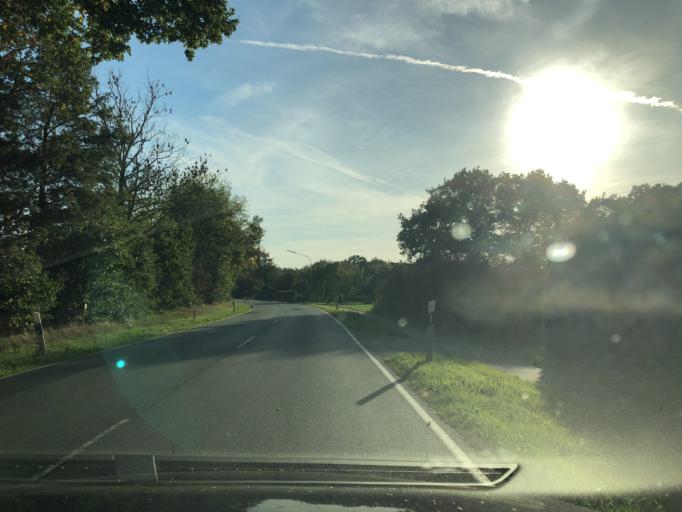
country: DE
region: Lower Saxony
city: Papenburg
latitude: 53.0558
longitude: 7.4068
